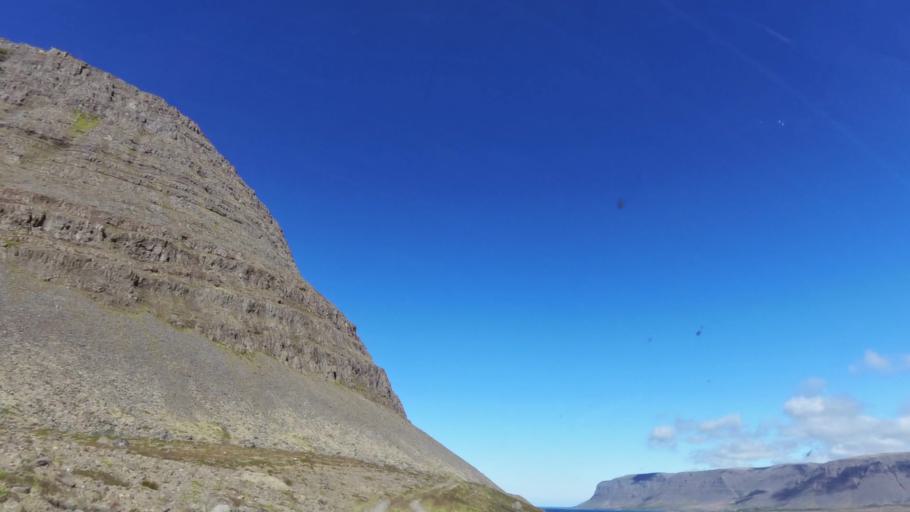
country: IS
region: West
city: Olafsvik
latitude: 65.6258
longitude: -23.8981
